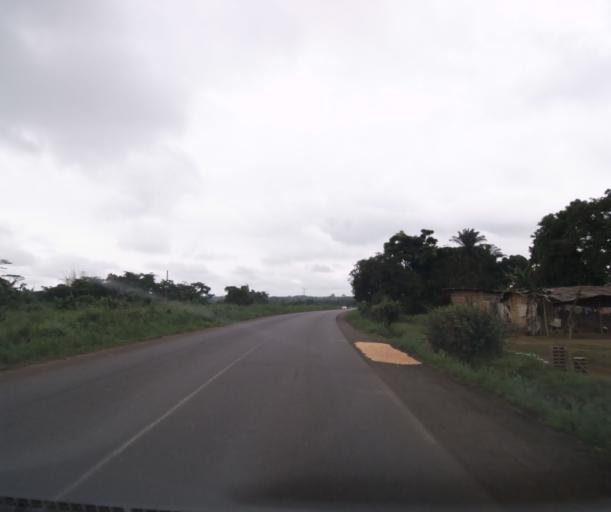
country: CM
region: Littoral
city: Edea
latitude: 3.7498
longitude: 10.1212
